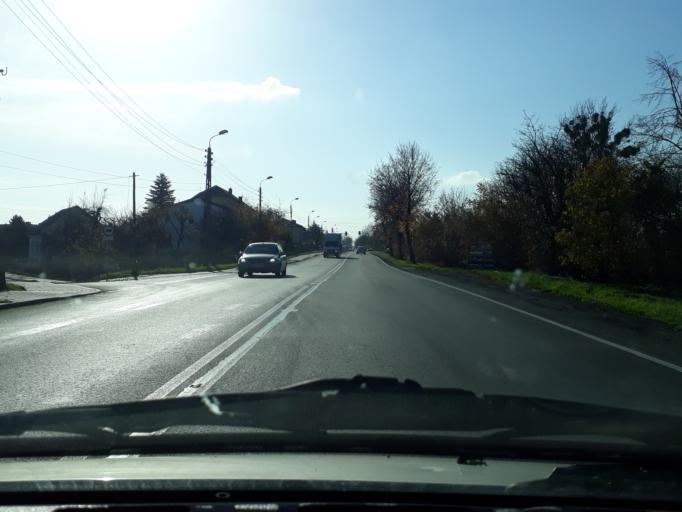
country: PL
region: Silesian Voivodeship
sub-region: Powiat tarnogorski
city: Tarnowskie Gory
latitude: 50.4342
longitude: 18.8443
